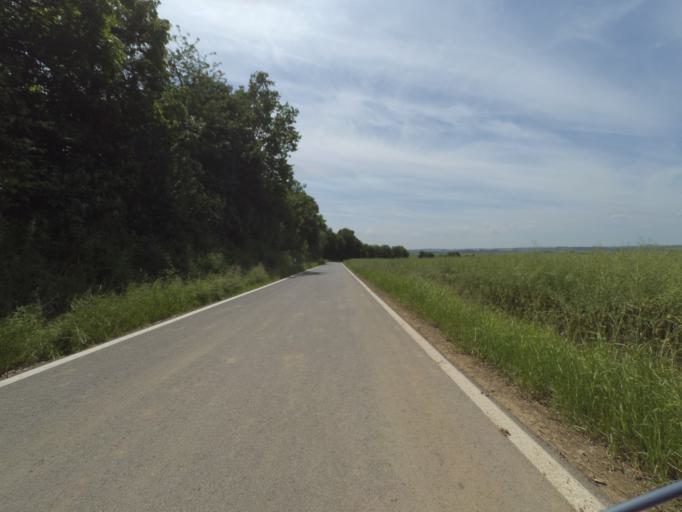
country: DE
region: Rheinland-Pfalz
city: Munstermaifeld
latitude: 50.2418
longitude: 7.3525
